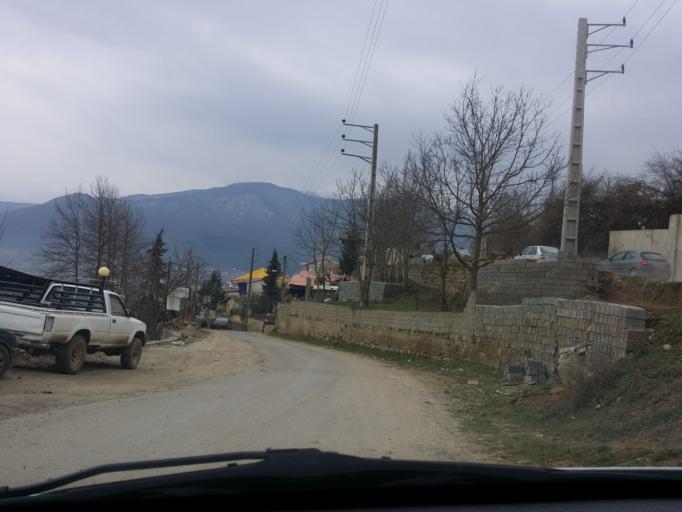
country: IR
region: Mazandaran
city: `Abbasabad
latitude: 36.5356
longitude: 51.1605
